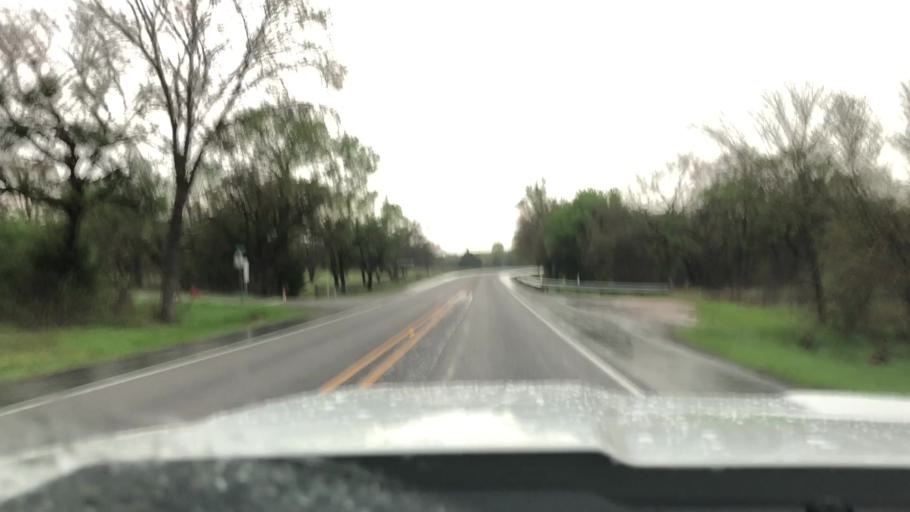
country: US
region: Texas
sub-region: Johnson County
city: Keene
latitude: 32.4236
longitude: -97.3190
